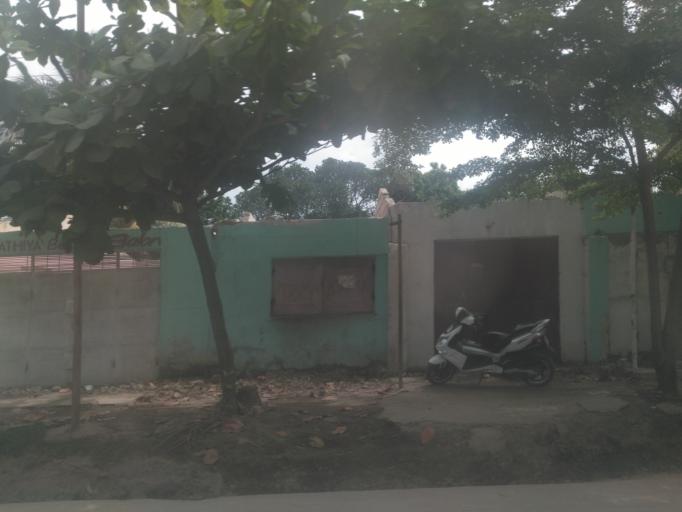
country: TZ
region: Zanzibar Urban/West
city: Zanzibar
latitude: -6.2093
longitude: 39.2165
